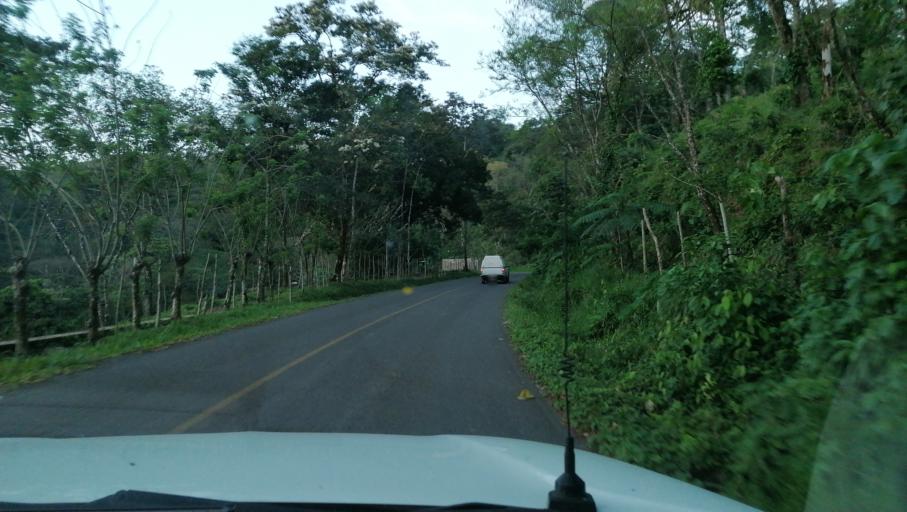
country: MX
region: Chiapas
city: Ostuacan
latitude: 17.4234
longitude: -93.3457
